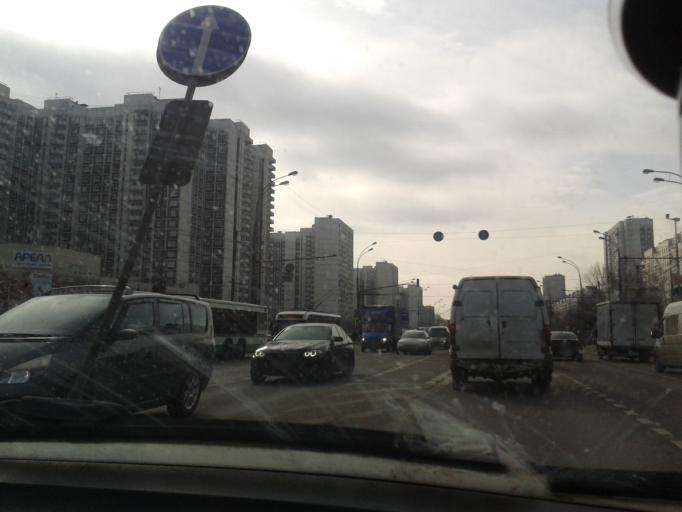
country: RU
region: Moscow
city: Lianozovo
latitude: 55.8988
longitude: 37.5869
